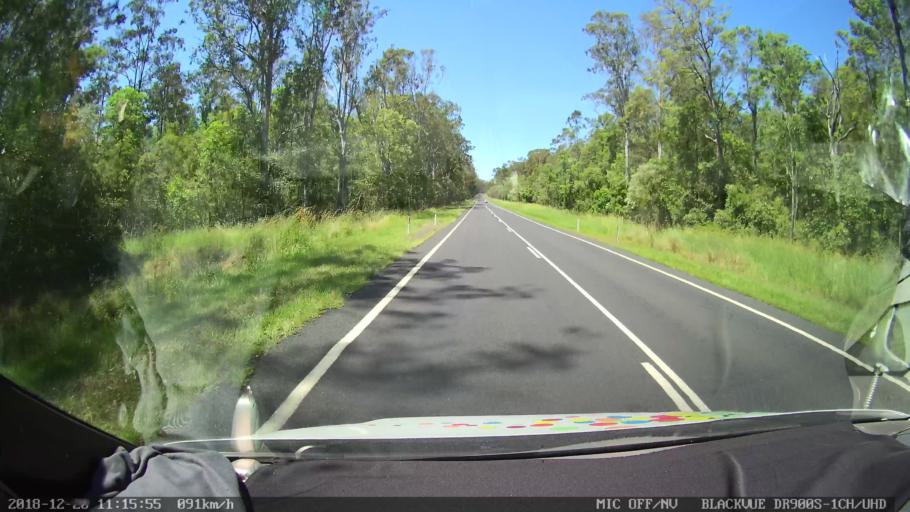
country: AU
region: New South Wales
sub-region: Richmond Valley
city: Casino
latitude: -29.0194
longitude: 153.0111
